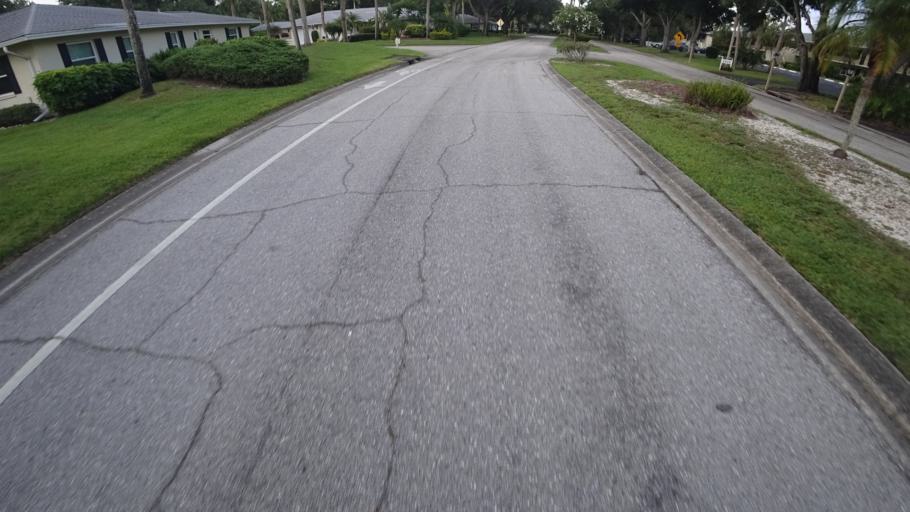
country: US
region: Florida
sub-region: Sarasota County
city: Desoto Lakes
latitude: 27.4175
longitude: -82.4945
